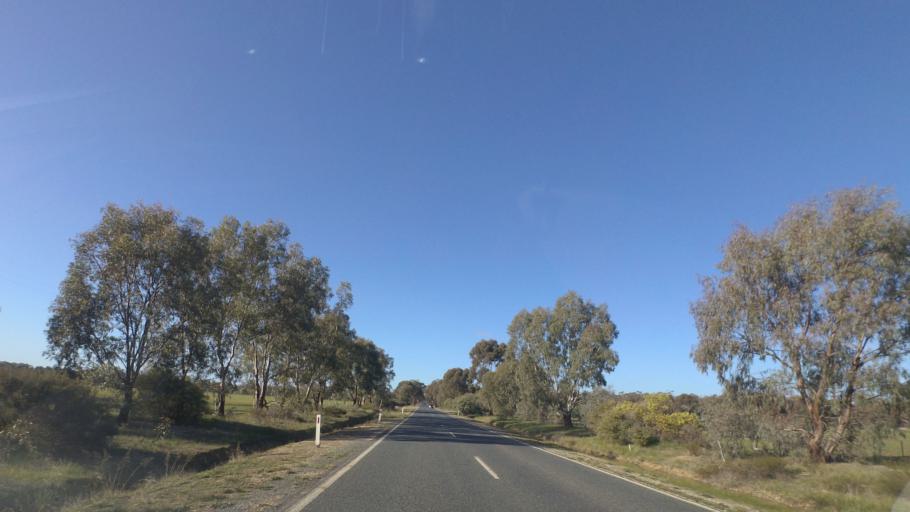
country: AU
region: Victoria
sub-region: Greater Bendigo
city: Epsom
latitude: -36.6751
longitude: 144.3963
